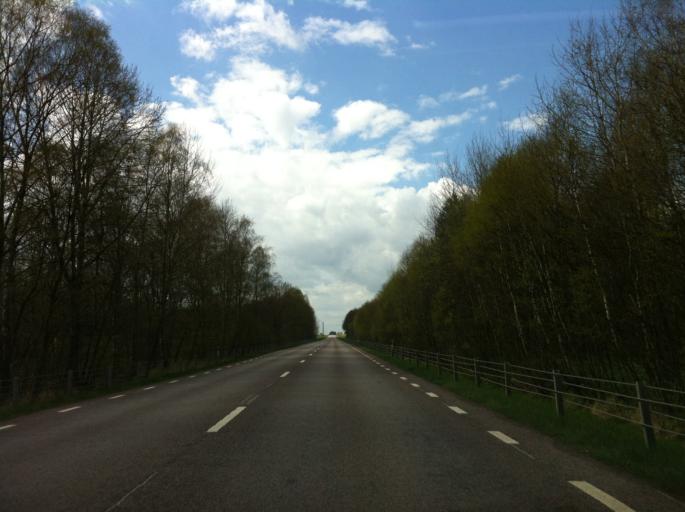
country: SE
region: Skane
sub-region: Eslovs Kommun
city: Stehag
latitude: 55.8533
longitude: 13.3917
